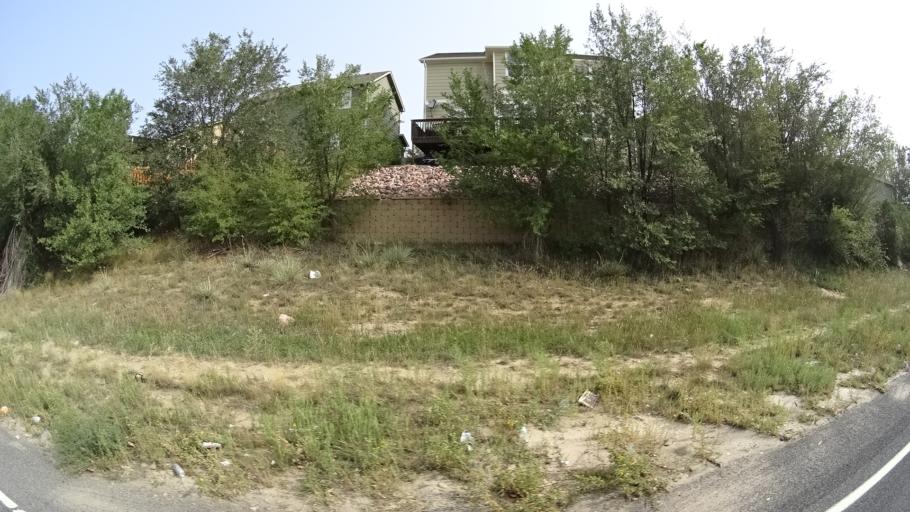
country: US
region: Colorado
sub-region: El Paso County
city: Stratmoor
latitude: 38.7999
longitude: -104.7791
